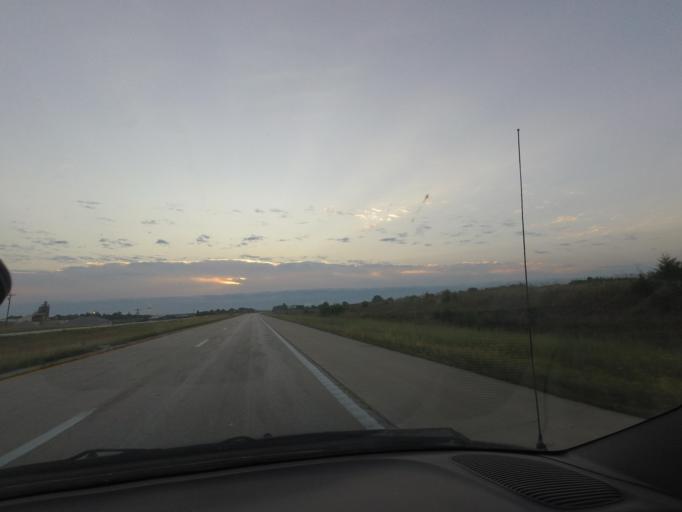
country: US
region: Missouri
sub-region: Macon County
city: Macon
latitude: 39.7552
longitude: -92.4397
